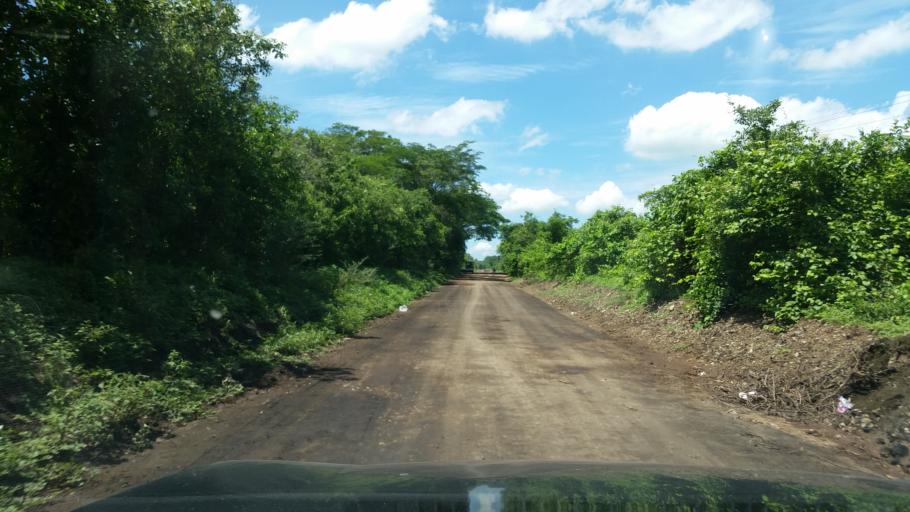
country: NI
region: Chinandega
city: El Viejo
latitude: 12.7562
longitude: -87.1336
